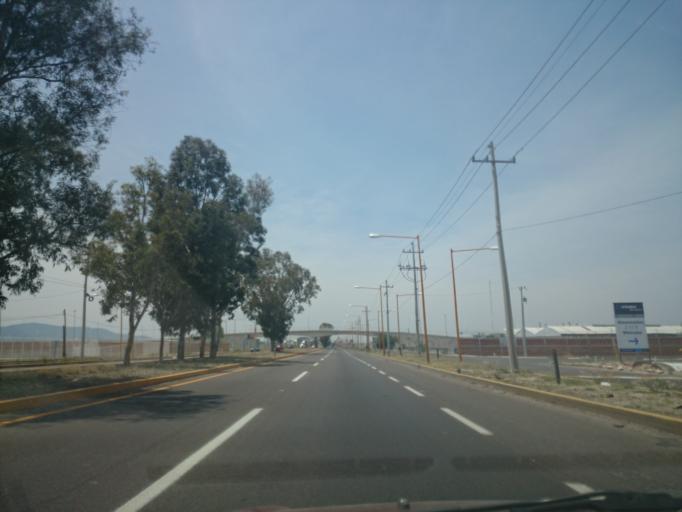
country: MX
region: Aguascalientes
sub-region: Aguascalientes
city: Penuelas (El Cienegal)
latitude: 21.7429
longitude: -102.2771
